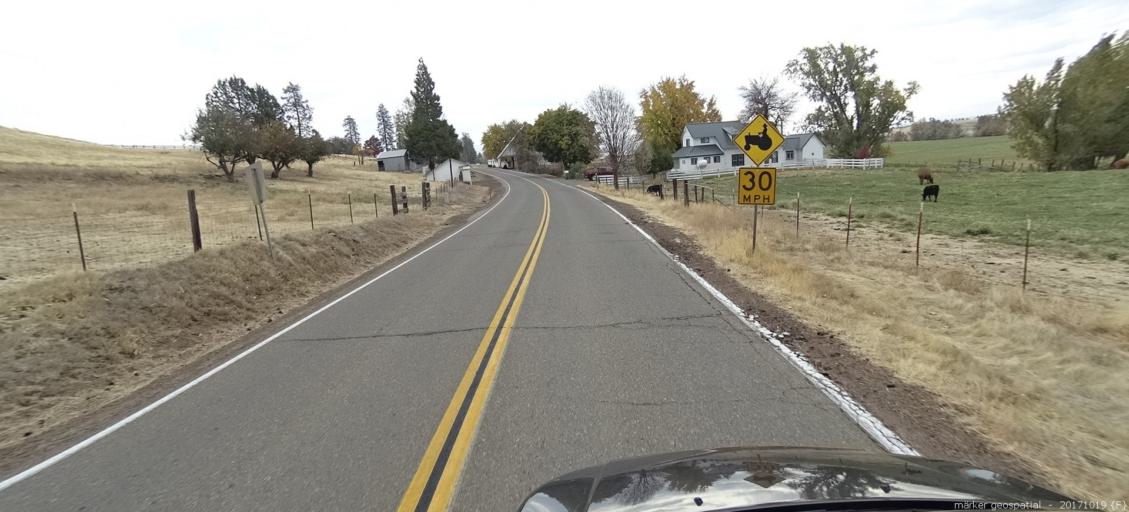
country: US
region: California
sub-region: Shasta County
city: Burney
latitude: 41.0542
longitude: -121.3608
